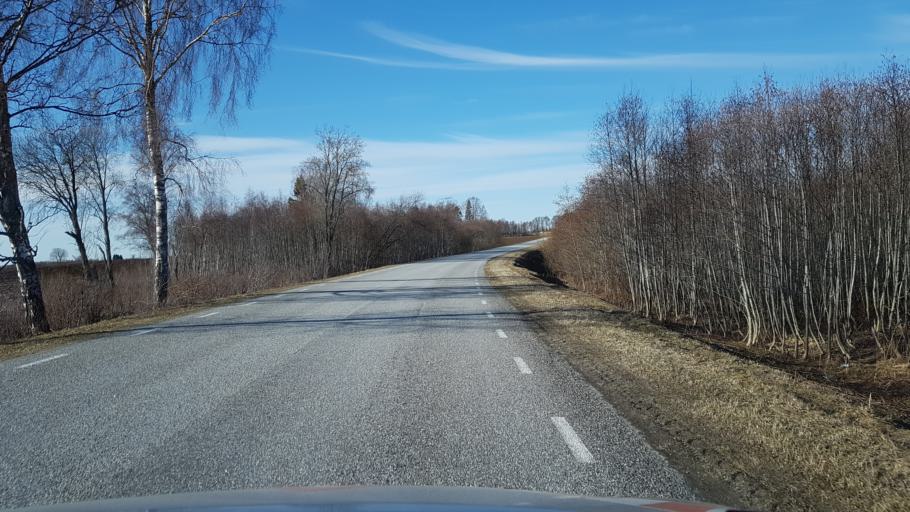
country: EE
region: Laeaene-Virumaa
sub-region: Kadrina vald
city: Kadrina
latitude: 59.3035
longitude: 26.1592
